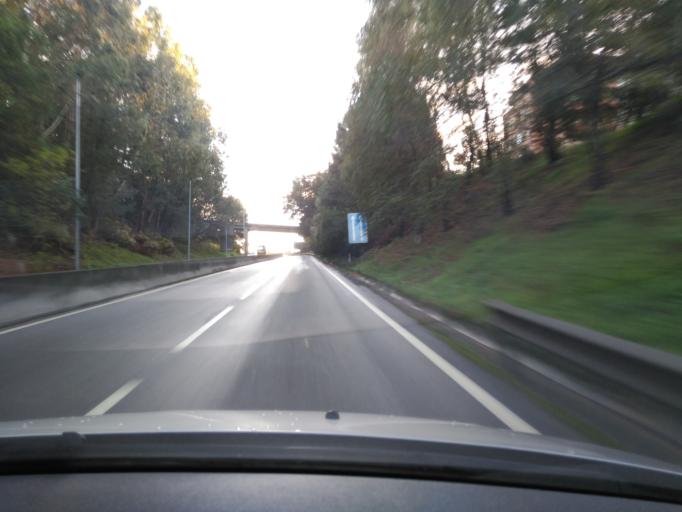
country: PT
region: Braga
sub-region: Guimaraes
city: Guimaraes
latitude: 41.4505
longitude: -8.3064
